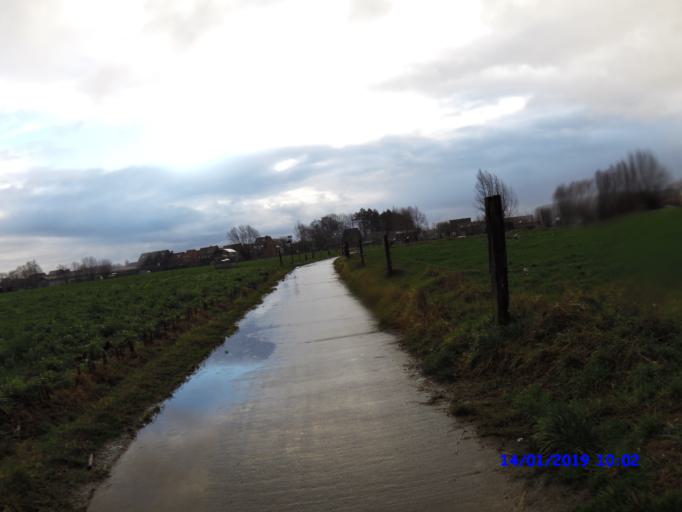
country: BE
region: Flanders
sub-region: Provincie Vlaams-Brabant
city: Opwijk
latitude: 50.9959
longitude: 4.1717
